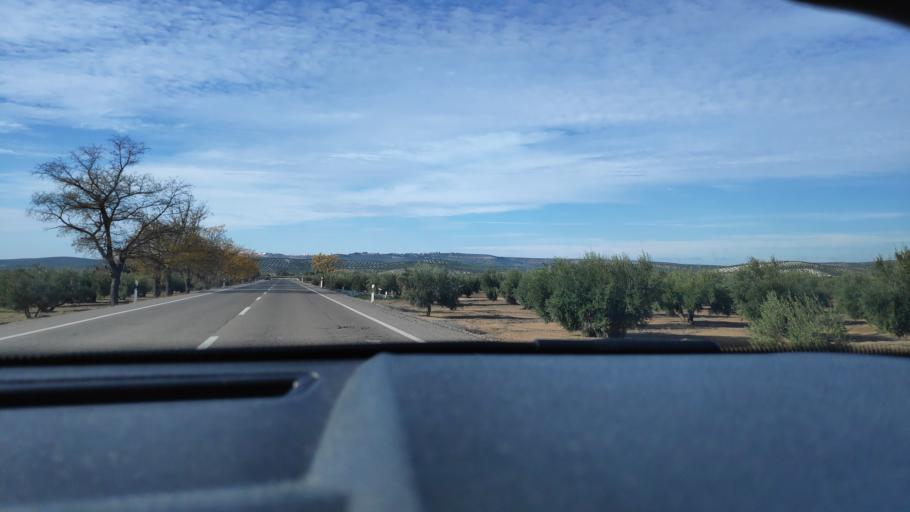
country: ES
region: Andalusia
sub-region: Provincia de Jaen
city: Higuera de Calatrava
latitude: 37.8445
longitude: -4.1173
